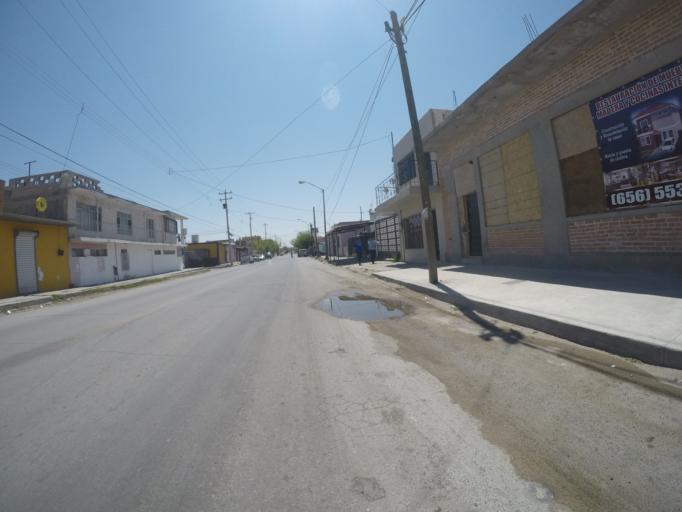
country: MX
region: Chihuahua
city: Ciudad Juarez
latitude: 31.7291
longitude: -106.4839
